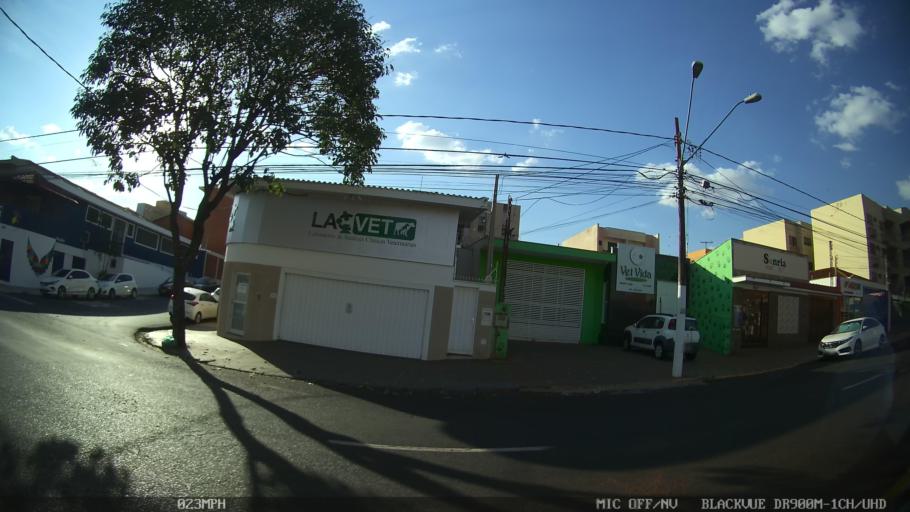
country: BR
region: Sao Paulo
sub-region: Ribeirao Preto
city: Ribeirao Preto
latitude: -21.1873
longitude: -47.7918
